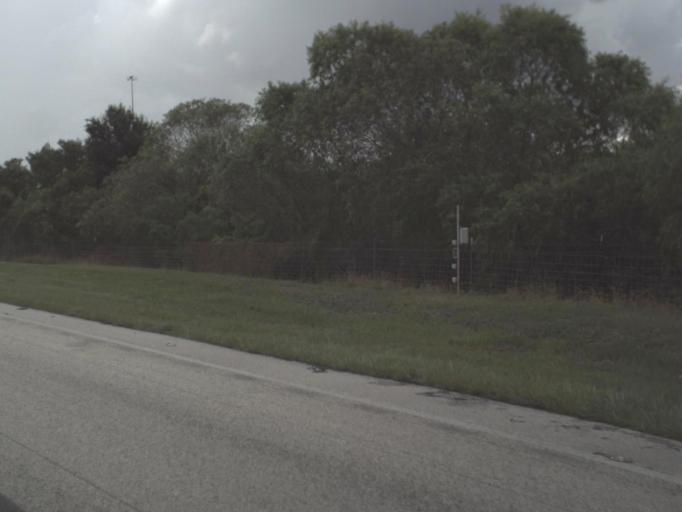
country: US
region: Florida
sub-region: Polk County
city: Polk City
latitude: 28.1746
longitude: -81.7623
